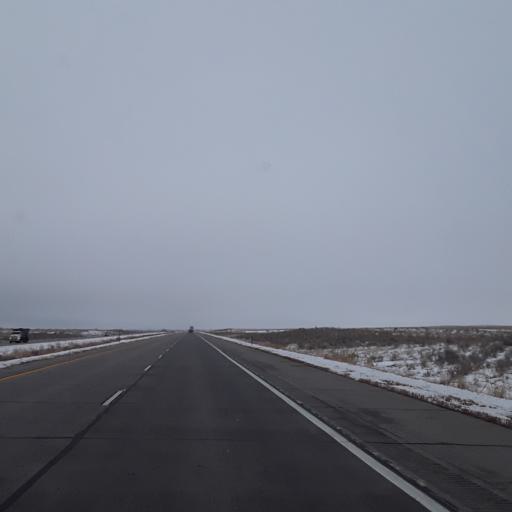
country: US
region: Colorado
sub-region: Logan County
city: Sterling
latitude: 40.5530
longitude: -103.2160
